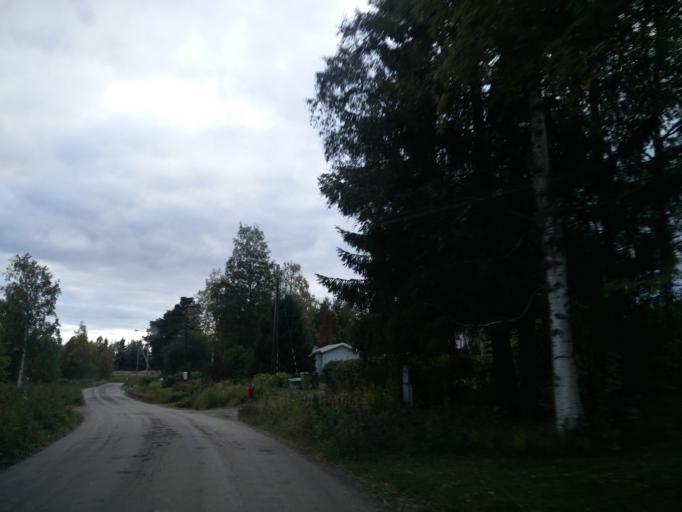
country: SE
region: Vaesternorrland
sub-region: Sundsvalls Kommun
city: Matfors
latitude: 62.3462
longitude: 17.0828
